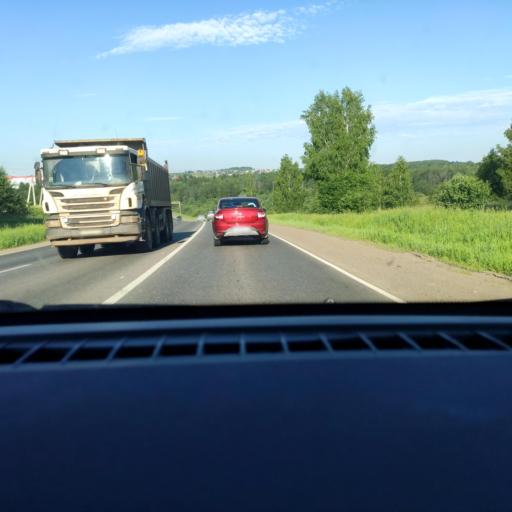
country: RU
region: Udmurtiya
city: Khokhryaki
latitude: 56.9141
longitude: 53.3924
